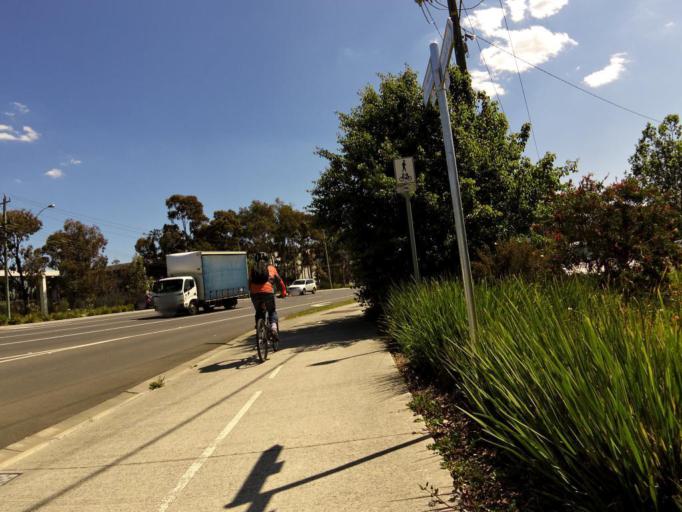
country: AU
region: Victoria
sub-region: Knox
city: Scoresby
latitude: -37.8989
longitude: 145.2301
